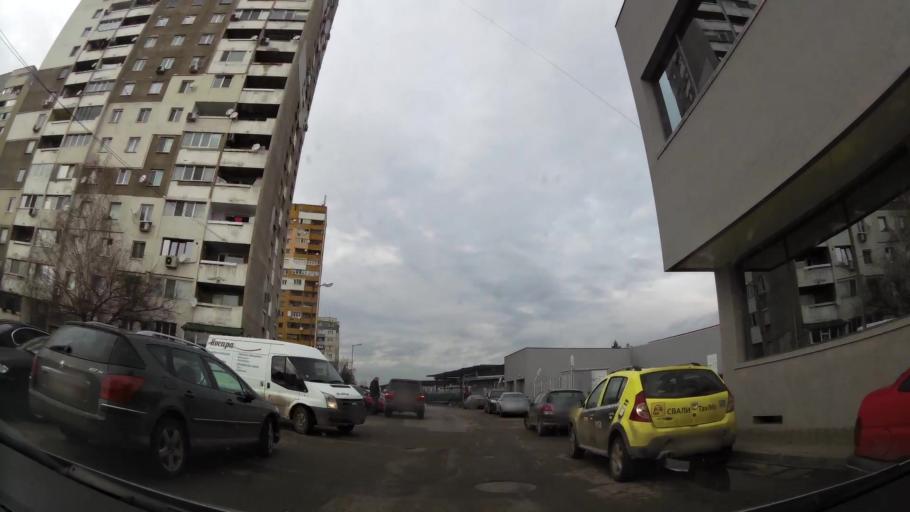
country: BG
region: Sofia-Capital
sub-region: Stolichna Obshtina
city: Sofia
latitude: 42.7437
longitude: 23.2829
